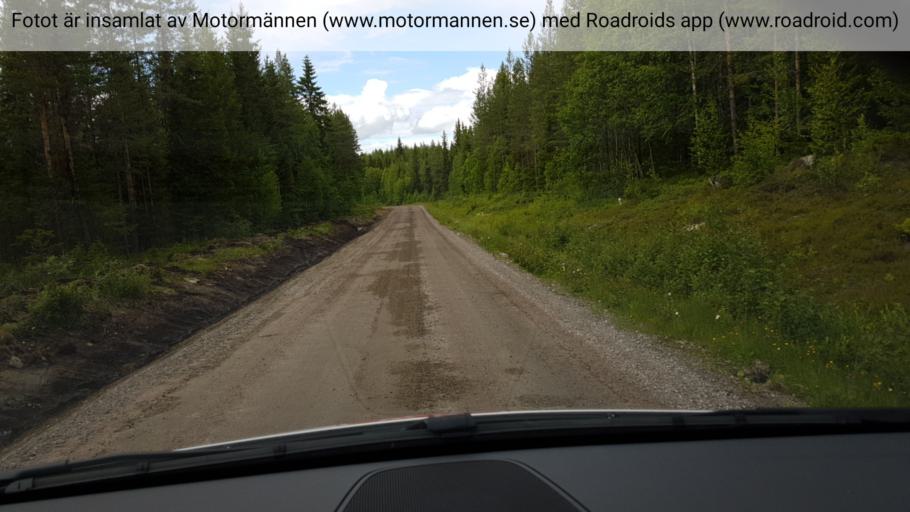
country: SE
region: Vaesterbotten
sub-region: Dorotea Kommun
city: Dorotea
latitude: 63.9699
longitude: 16.0660
